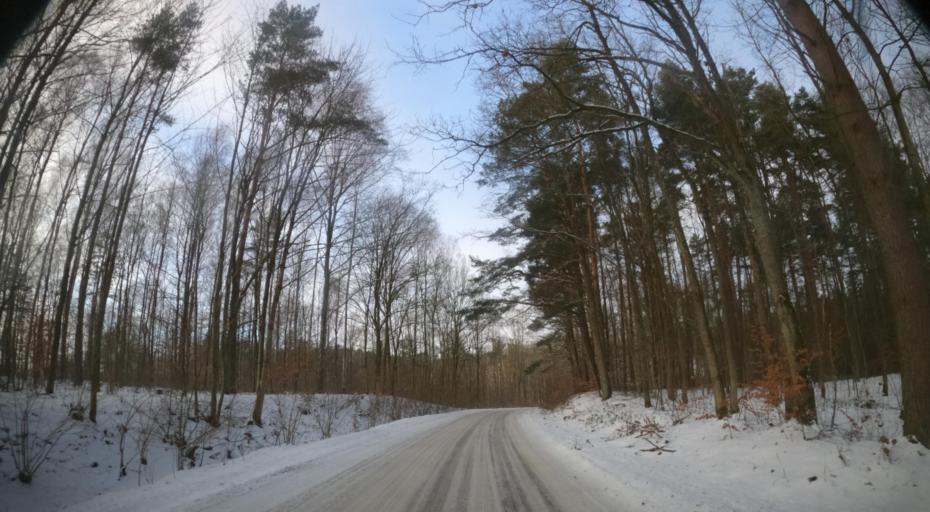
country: PL
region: West Pomeranian Voivodeship
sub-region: Powiat slawienski
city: Darlowo
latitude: 54.2839
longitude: 16.4462
